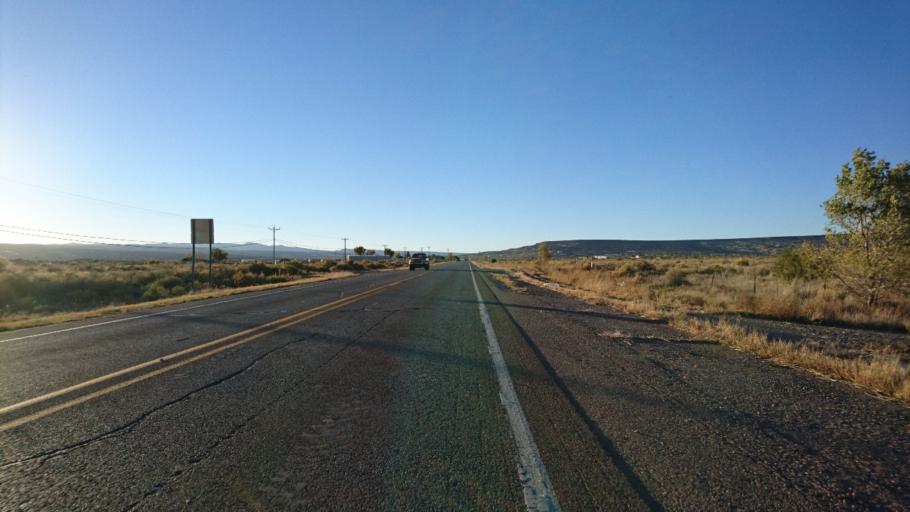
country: US
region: New Mexico
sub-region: Cibola County
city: Grants
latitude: 35.1321
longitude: -107.8133
